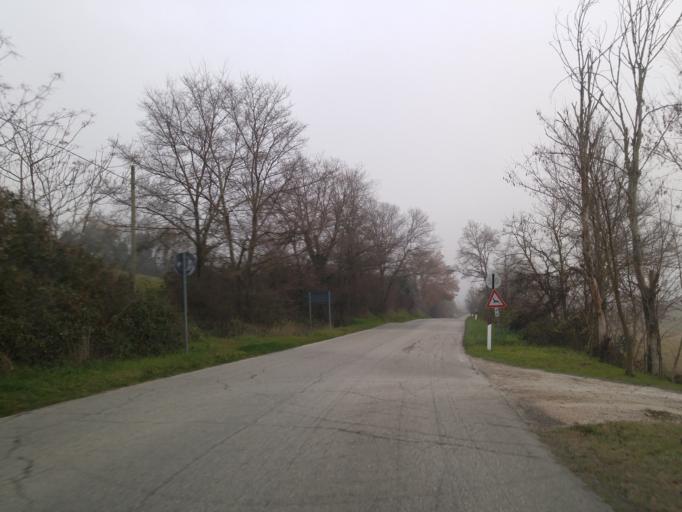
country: IT
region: The Marches
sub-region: Provincia di Pesaro e Urbino
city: Isola del Piano
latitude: 43.7371
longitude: 12.7947
